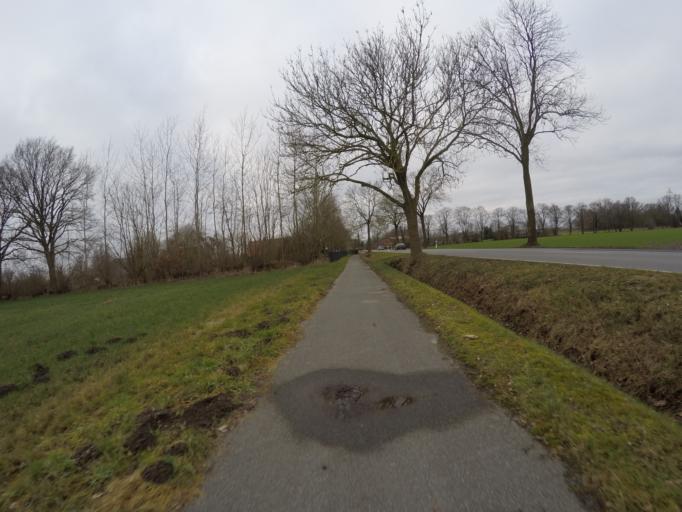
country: DE
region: Schleswig-Holstein
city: Hemdingen
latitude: 53.7629
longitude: 9.8546
